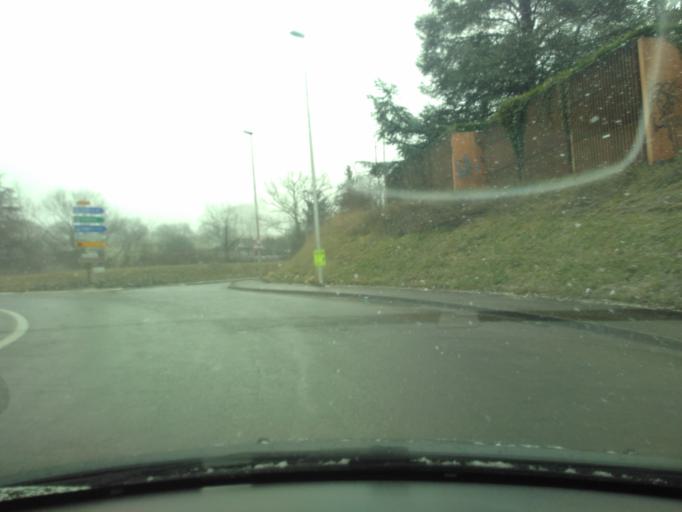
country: FR
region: Rhone-Alpes
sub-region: Departement de la Haute-Savoie
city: Saint-Julien-en-Genevois
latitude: 46.1376
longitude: 6.0778
